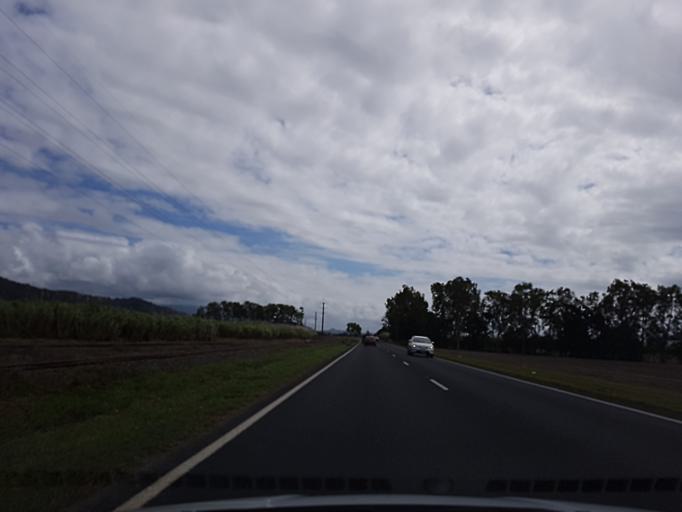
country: AU
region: Queensland
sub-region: Cairns
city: Port Douglas
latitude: -16.5100
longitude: 145.4426
